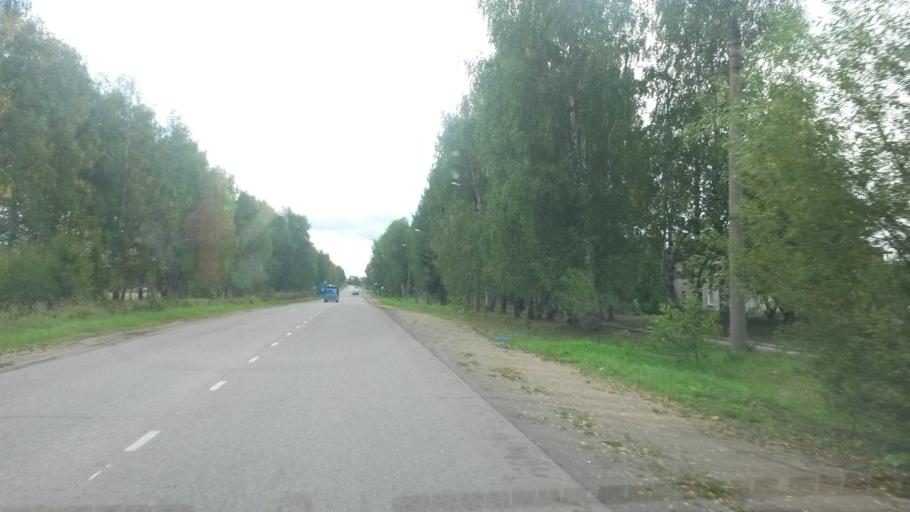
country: RU
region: Ivanovo
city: Zavolzhsk
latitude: 57.4732
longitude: 42.1565
